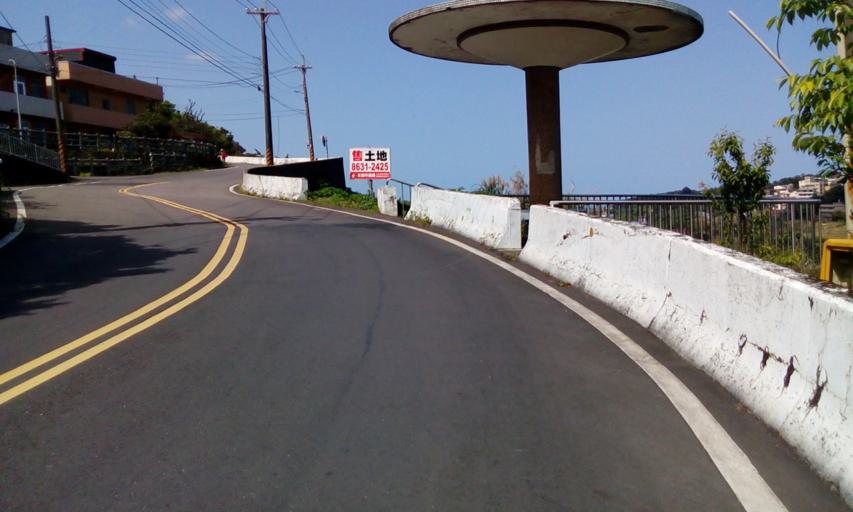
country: TW
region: Taipei
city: Taipei
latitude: 25.2015
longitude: 121.4807
